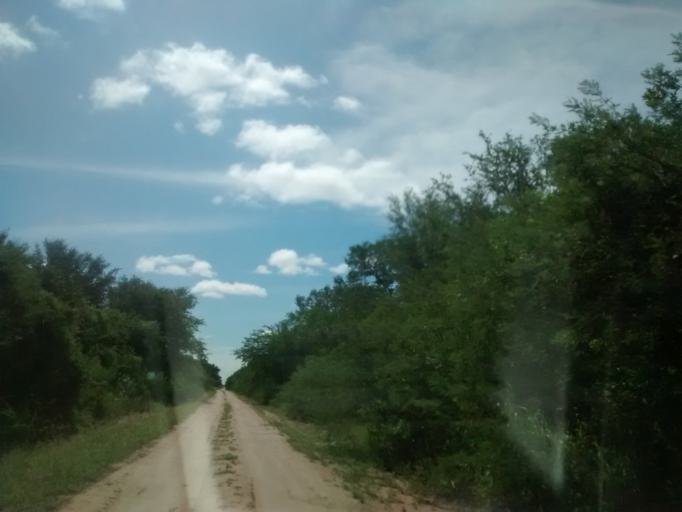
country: AR
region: Chaco
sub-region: Departamento de Quitilipi
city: Quitilipi
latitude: -26.7744
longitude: -60.2488
